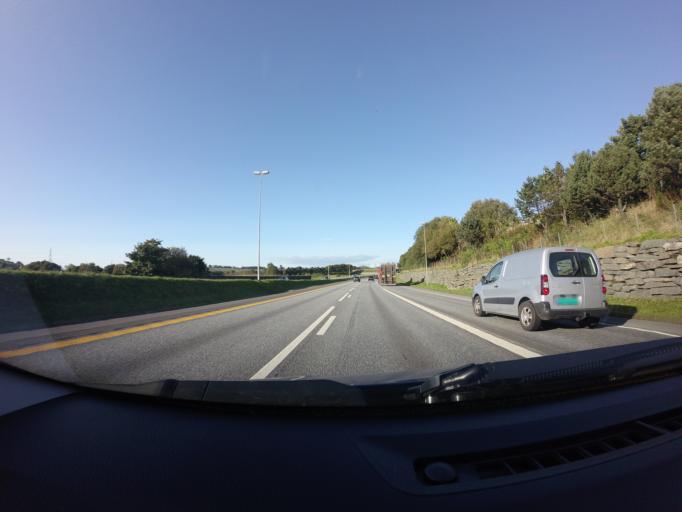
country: NO
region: Rogaland
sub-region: Sandnes
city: Sandnes
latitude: 58.8654
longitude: 5.7119
